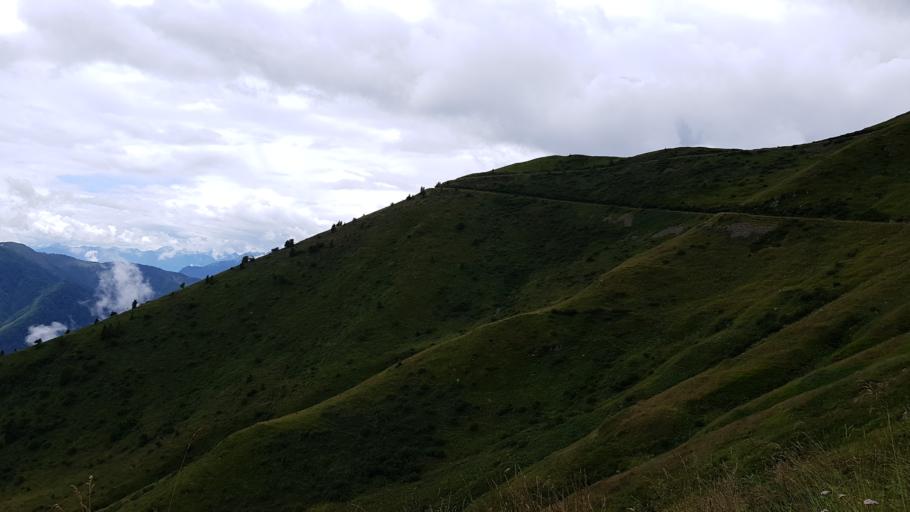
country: IT
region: Friuli Venezia Giulia
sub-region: Provincia di Udine
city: Cercivento
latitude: 46.5559
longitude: 12.9799
